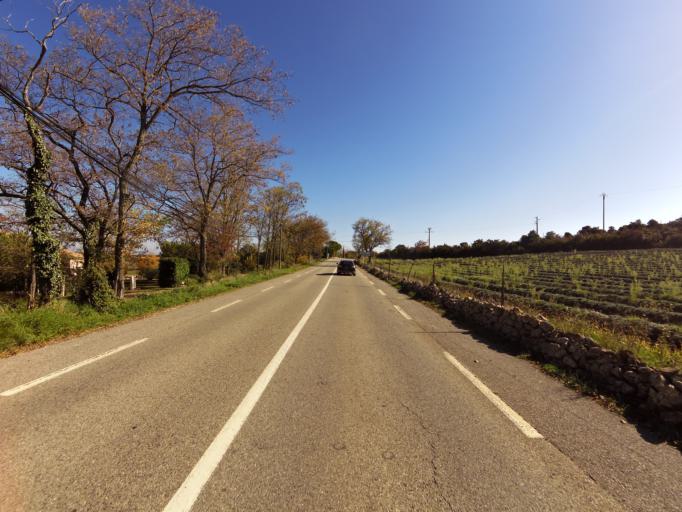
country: FR
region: Languedoc-Roussillon
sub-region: Departement du Gard
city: Saint-Julien-de-Peyrolas
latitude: 44.3917
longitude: 4.5087
